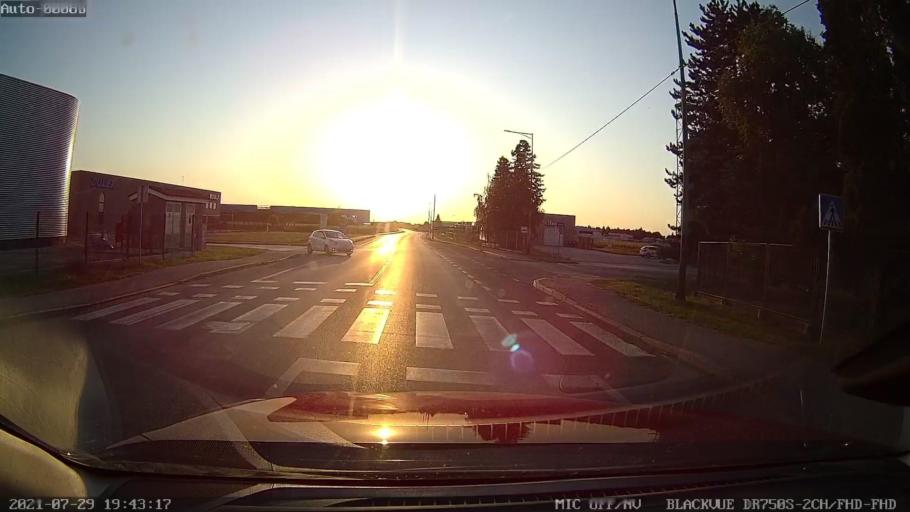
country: HR
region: Varazdinska
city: Ludbreg
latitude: 46.2556
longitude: 16.6058
